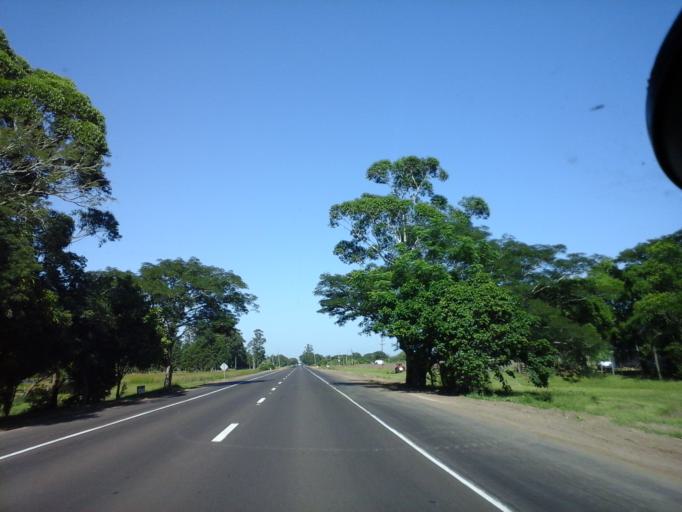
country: AR
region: Corrientes
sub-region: Departamento de Itati
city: Itati
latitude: -27.3666
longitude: -58.3329
